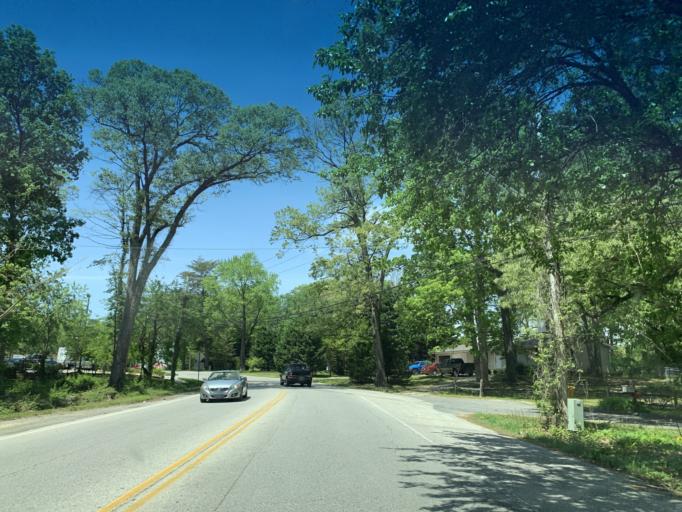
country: US
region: Maryland
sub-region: Anne Arundel County
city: Severna Park
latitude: 39.0800
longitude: -76.5460
